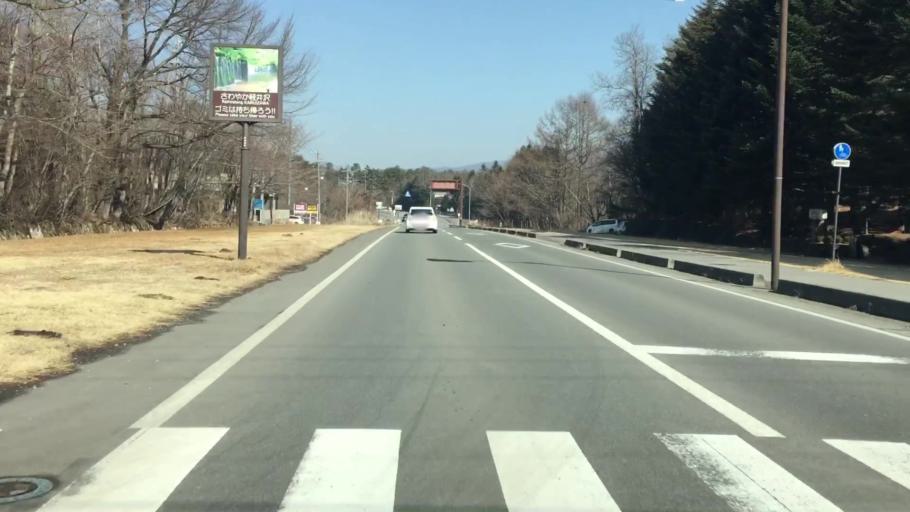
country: JP
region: Nagano
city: Saku
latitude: 36.3166
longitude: 138.6311
